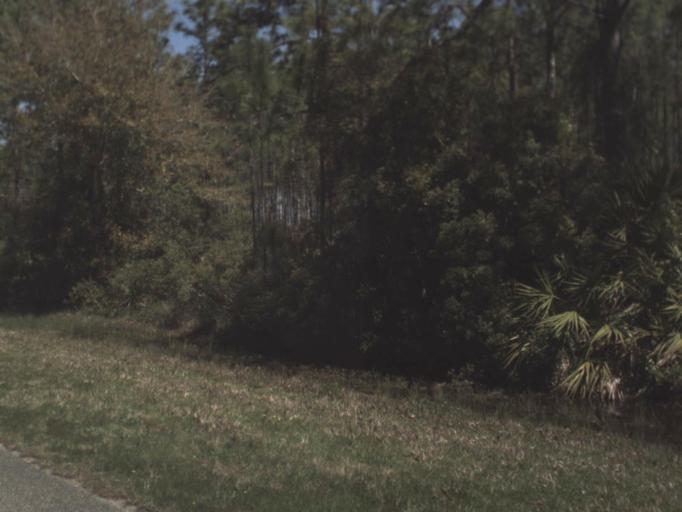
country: US
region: Florida
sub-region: Gulf County
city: Port Saint Joe
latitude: 29.7673
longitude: -85.2626
